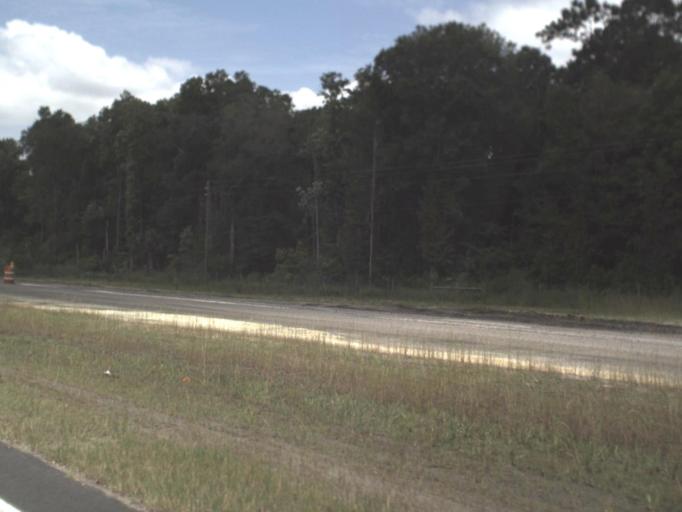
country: US
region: Florida
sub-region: Nassau County
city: Callahan
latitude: 30.5415
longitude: -81.8510
